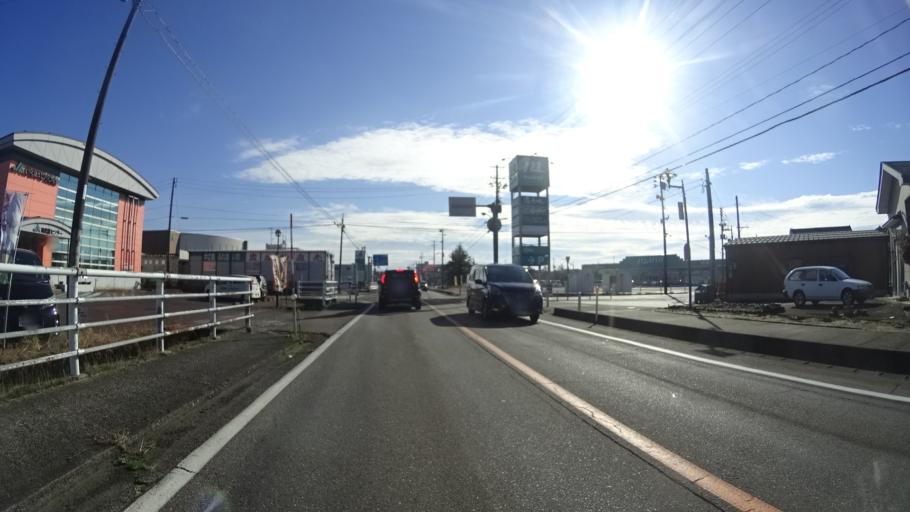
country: JP
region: Niigata
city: Mitsuke
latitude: 37.5482
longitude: 138.8753
